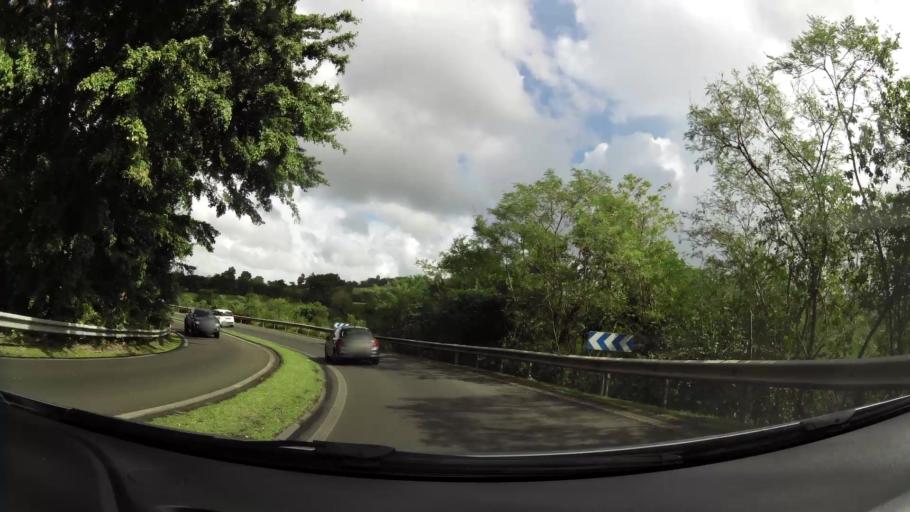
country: MQ
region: Martinique
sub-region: Martinique
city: Sainte-Luce
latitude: 14.5024
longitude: -60.9797
